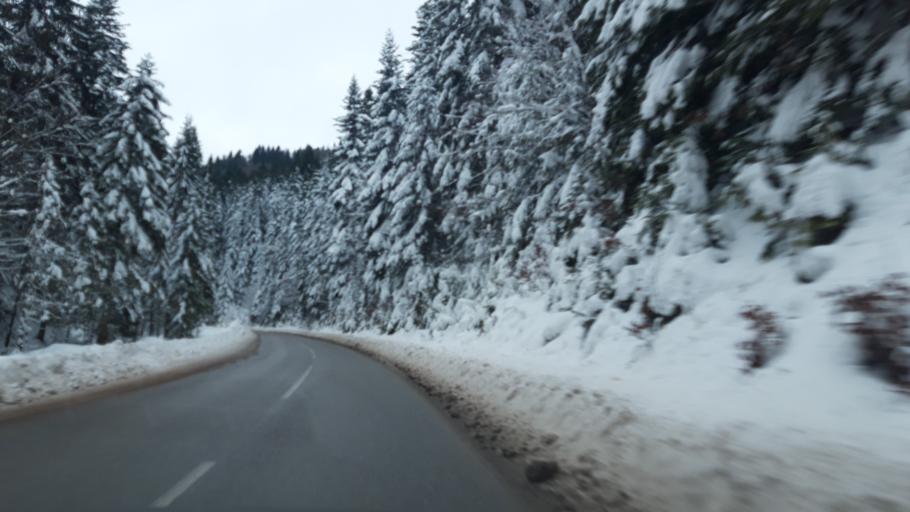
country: BA
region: Republika Srpska
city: Koran
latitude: 43.7521
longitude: 18.5506
